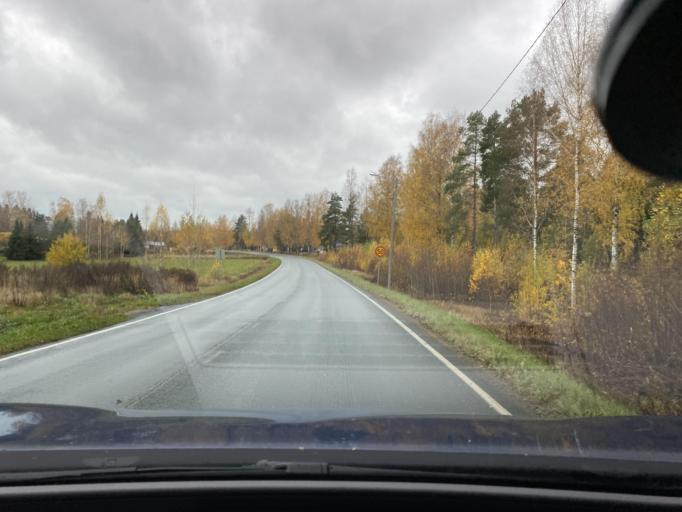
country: FI
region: Satakunta
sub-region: Pori
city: Kokemaeki
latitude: 61.2657
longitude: 22.4043
